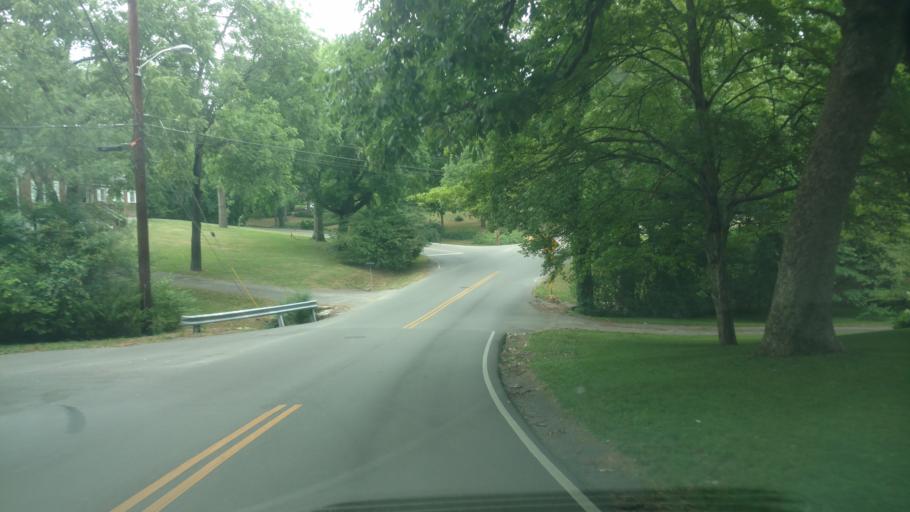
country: US
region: Tennessee
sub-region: Davidson County
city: Lakewood
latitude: 36.2170
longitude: -86.7108
